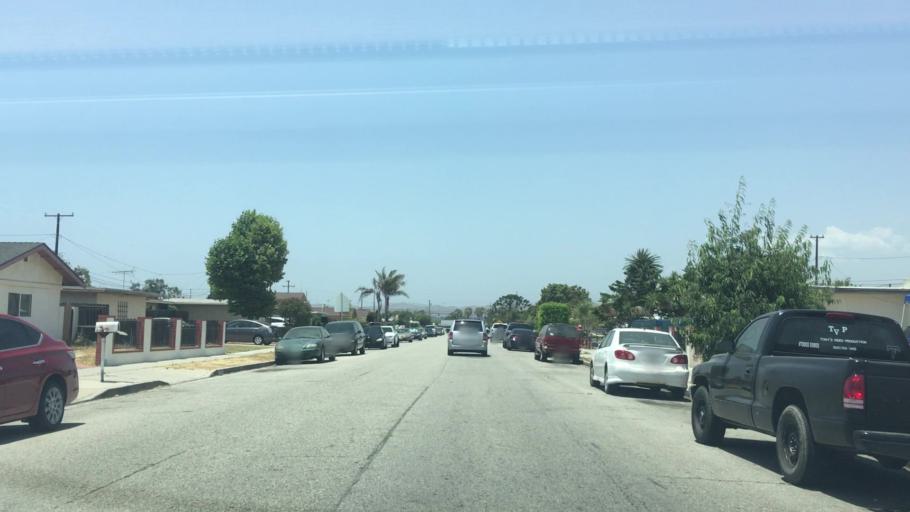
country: US
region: California
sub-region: Ventura County
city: El Rio
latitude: 34.2415
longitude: -119.1602
